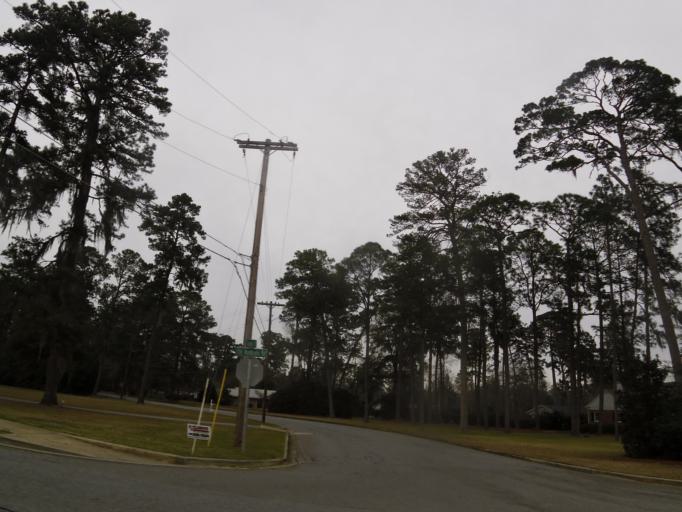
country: US
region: Georgia
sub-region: Thomas County
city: Thomasville
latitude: 30.8247
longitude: -83.9674
